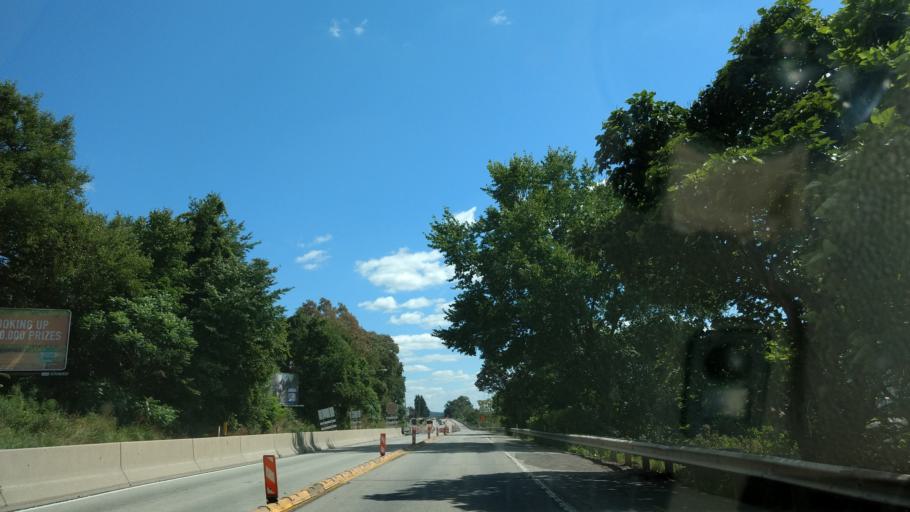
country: US
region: Pennsylvania
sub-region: Beaver County
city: Conway
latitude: 40.6669
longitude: -80.2425
